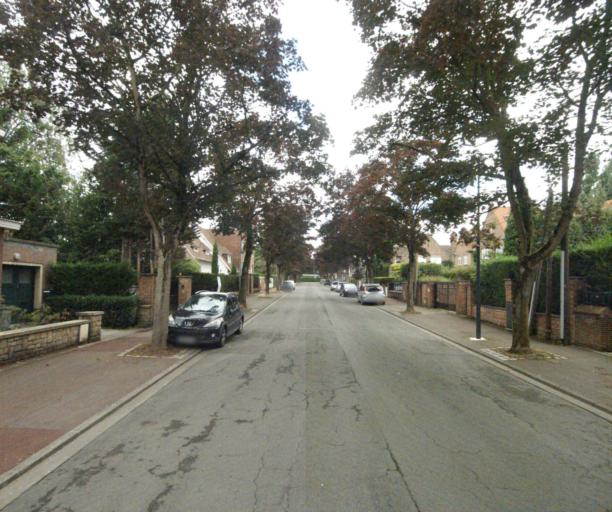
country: FR
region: Nord-Pas-de-Calais
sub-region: Departement du Nord
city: Roubaix
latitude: 50.6779
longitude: 3.1704
